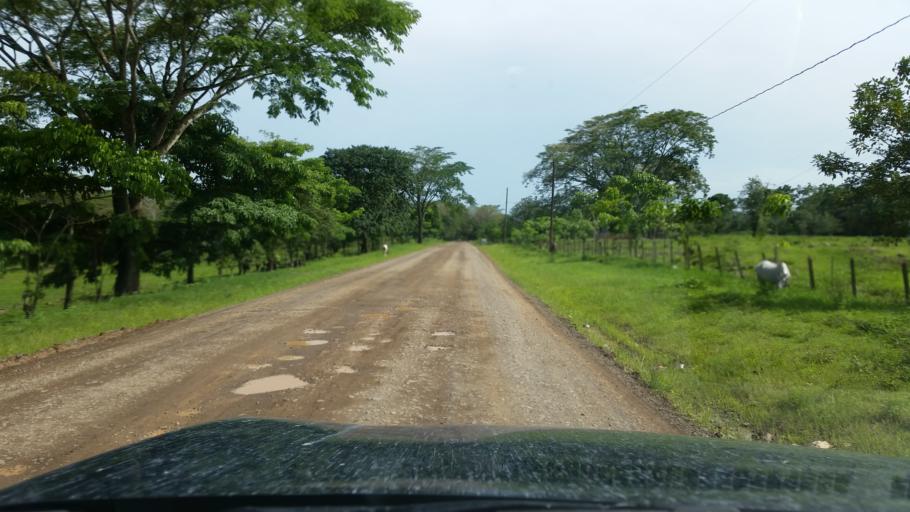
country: NI
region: Atlantico Norte (RAAN)
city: Siuna
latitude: 13.7086
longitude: -84.7765
